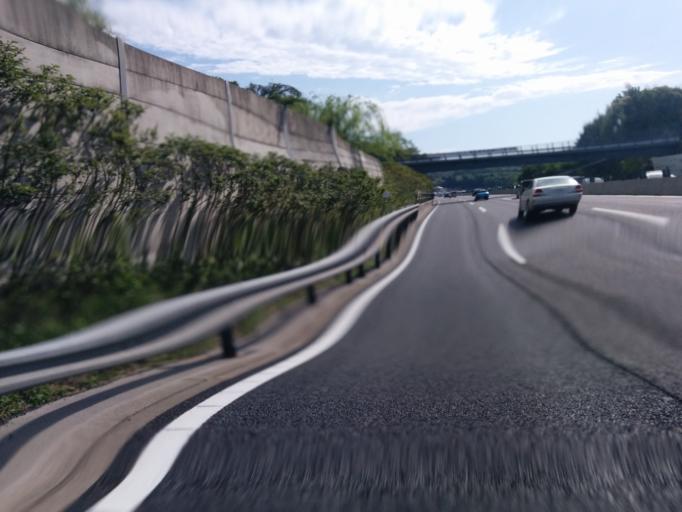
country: JP
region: Mie
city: Yokkaichi
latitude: 35.0082
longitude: 136.5788
